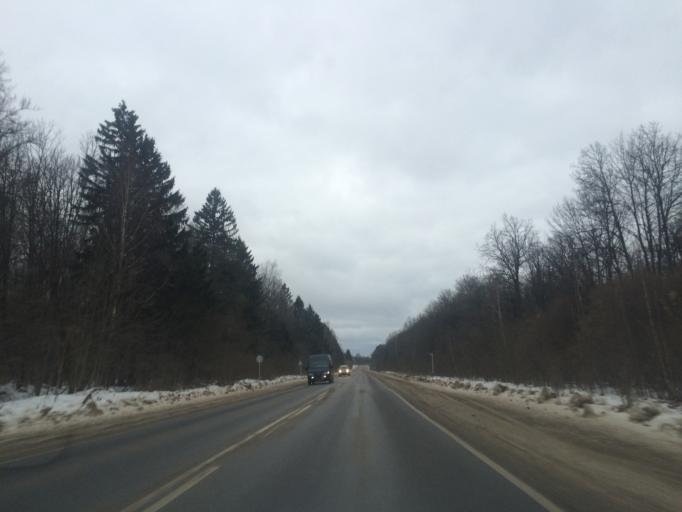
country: RU
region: Tula
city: Odoyev
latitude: 54.0067
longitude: 36.7923
